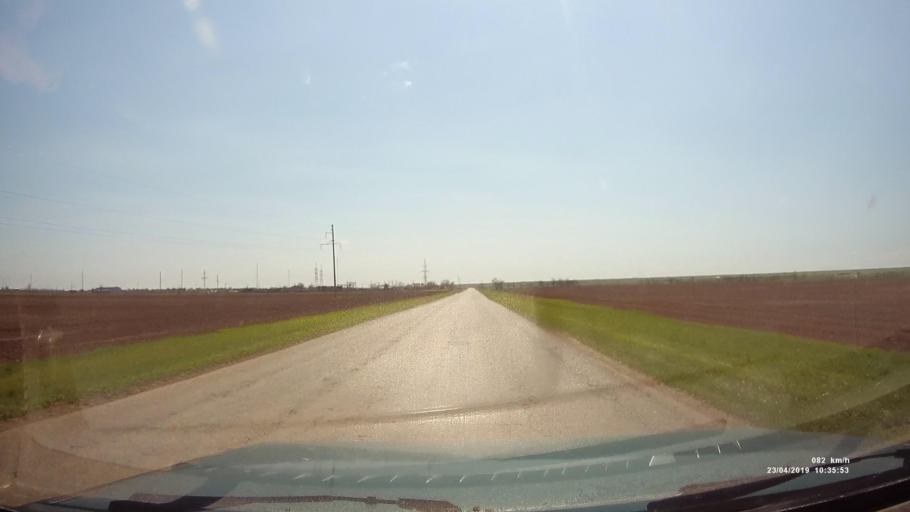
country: RU
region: Kalmykiya
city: Yashalta
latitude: 46.5498
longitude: 42.6296
